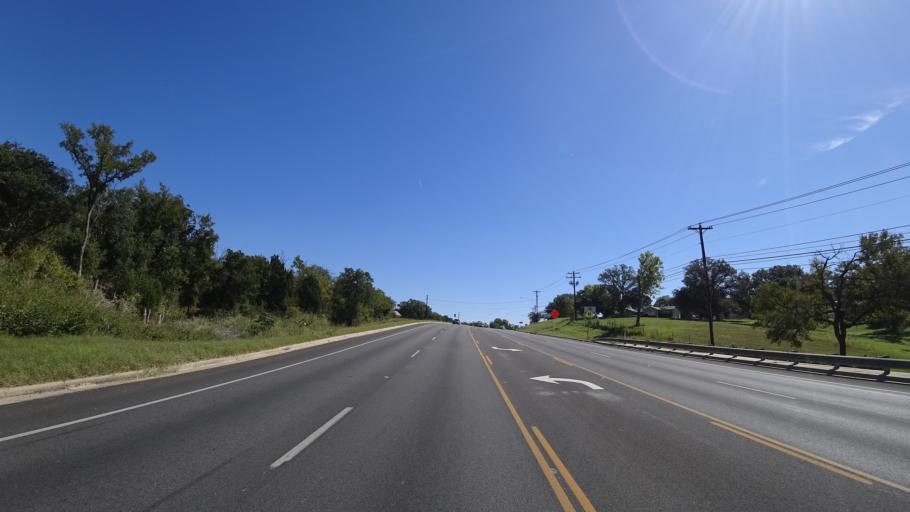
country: US
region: Texas
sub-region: Travis County
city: Hornsby Bend
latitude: 30.2781
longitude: -97.6404
